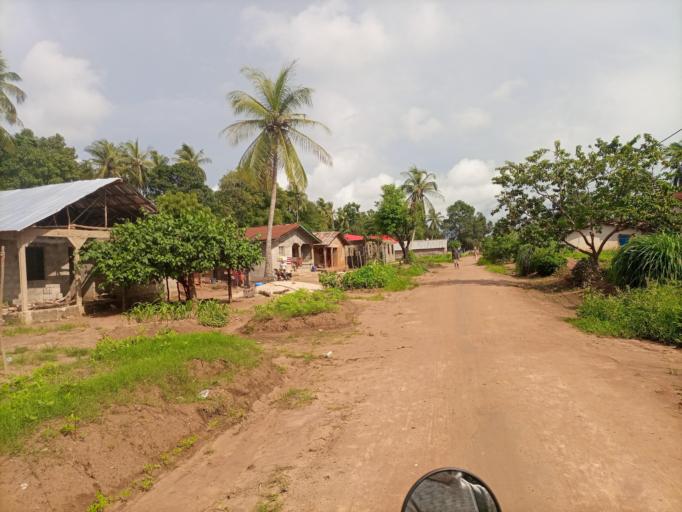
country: SL
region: Northern Province
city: Masoyila
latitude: 8.6179
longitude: -13.1716
